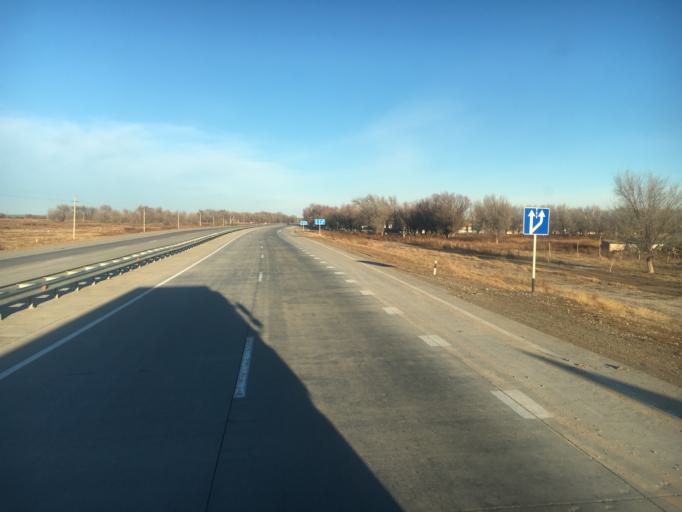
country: KZ
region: Ongtustik Qazaqstan
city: Turkestan
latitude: 43.1437
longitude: 68.5793
